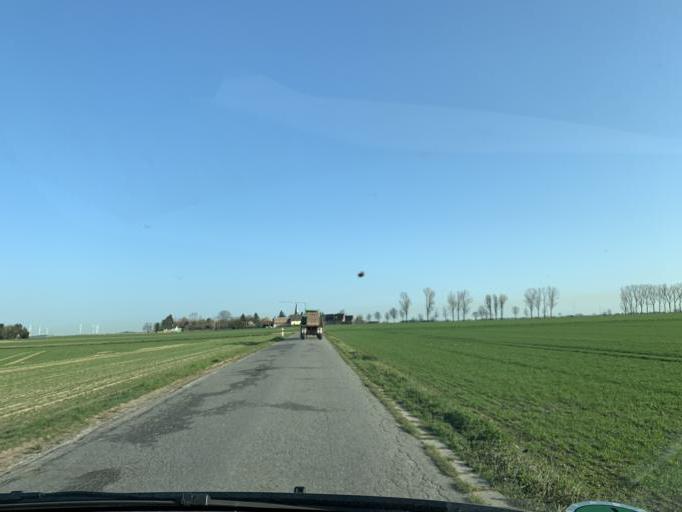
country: DE
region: North Rhine-Westphalia
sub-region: Regierungsbezirk Koln
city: Titz
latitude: 50.9828
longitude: 6.4624
